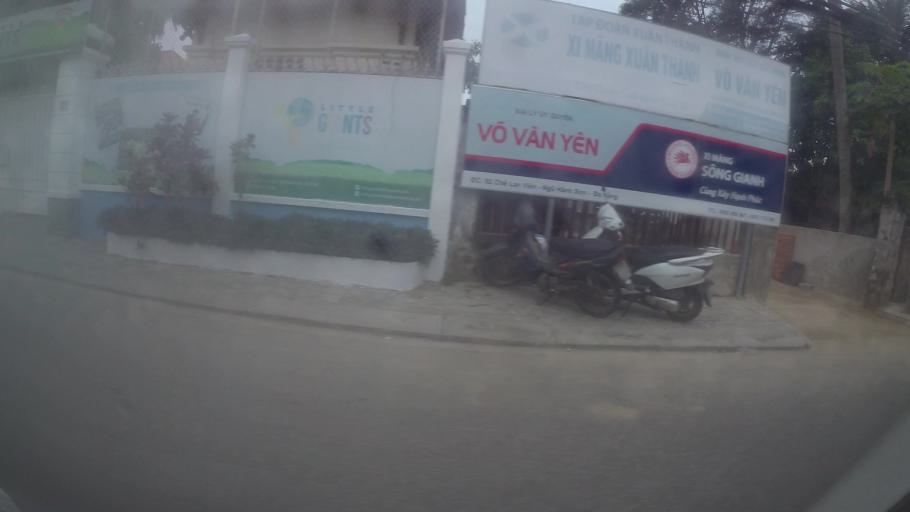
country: VN
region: Da Nang
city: Son Tra
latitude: 16.0434
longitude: 108.2451
